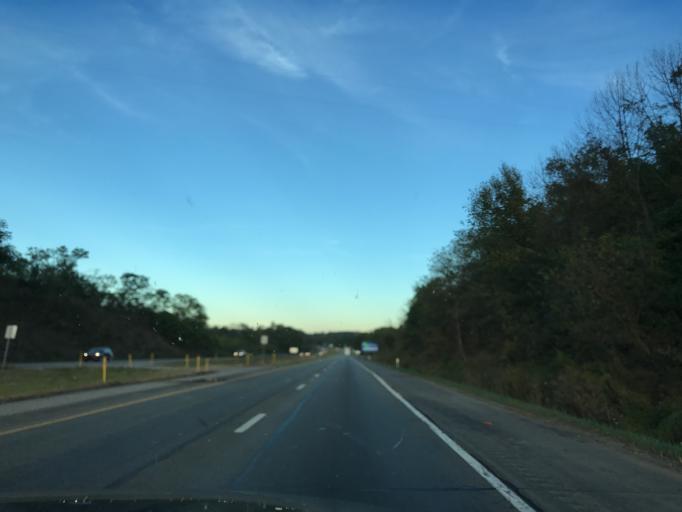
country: US
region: West Virginia
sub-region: Ohio County
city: West Liberty
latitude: 40.0956
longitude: -80.5193
